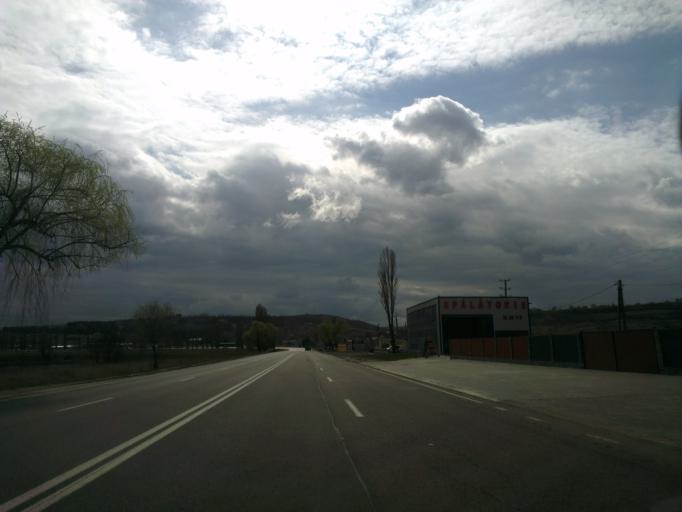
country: MD
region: Laloveni
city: Ialoveni
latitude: 46.9156
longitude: 28.6898
